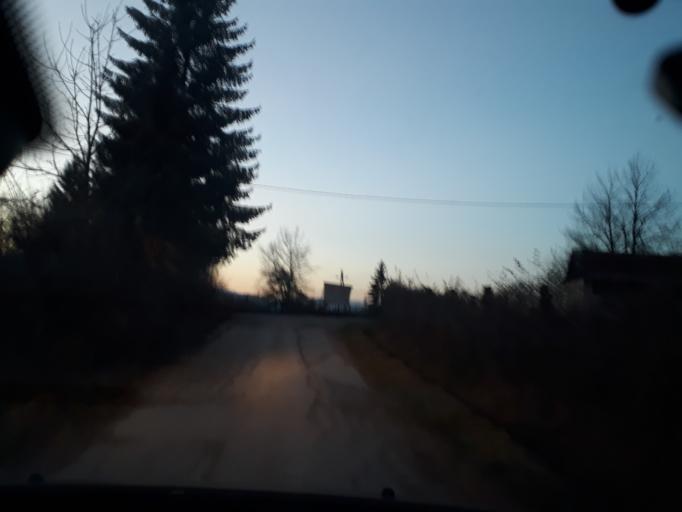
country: BA
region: Federation of Bosnia and Herzegovina
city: Hadzici
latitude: 43.8864
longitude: 18.1866
